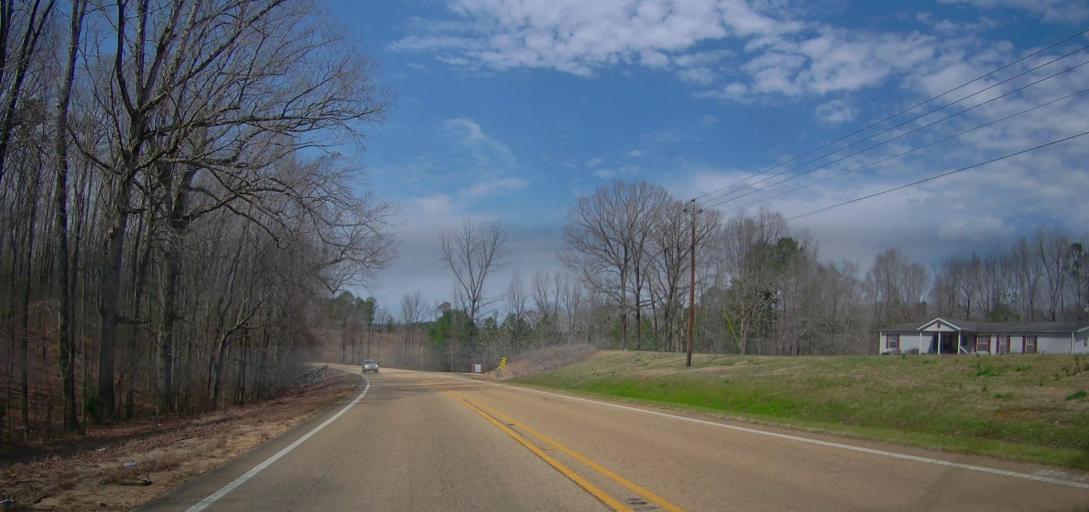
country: US
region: Mississippi
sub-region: Union County
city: New Albany
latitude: 34.6132
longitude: -89.1497
